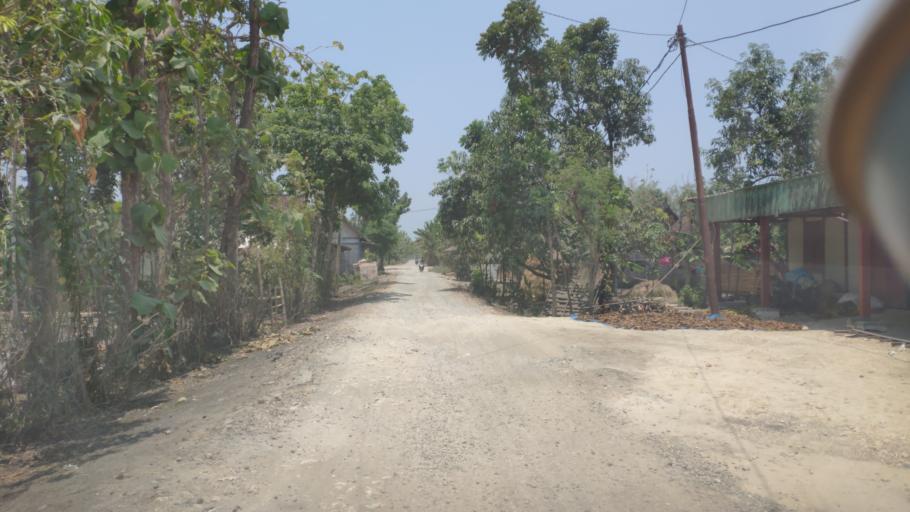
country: ID
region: Central Java
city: Mendenrejo
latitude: -7.2272
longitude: 111.4406
